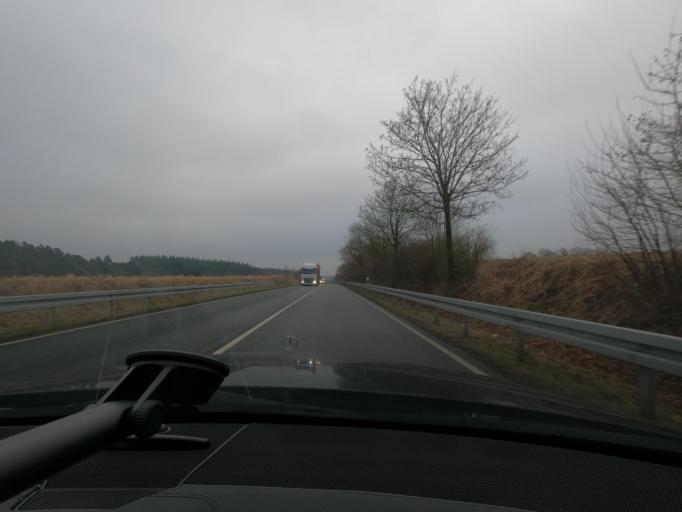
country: DE
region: Hesse
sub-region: Regierungsbezirk Kassel
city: Bad Arolsen
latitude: 51.4462
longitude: 9.0165
